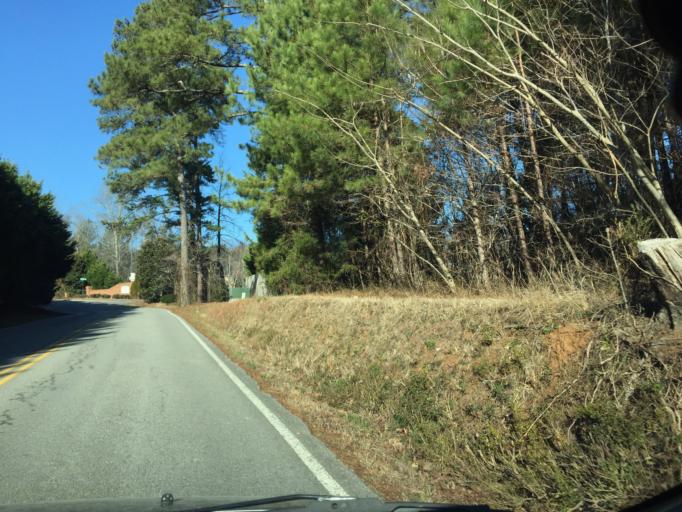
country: US
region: Tennessee
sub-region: Hamilton County
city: Collegedale
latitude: 35.0488
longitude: -85.0757
